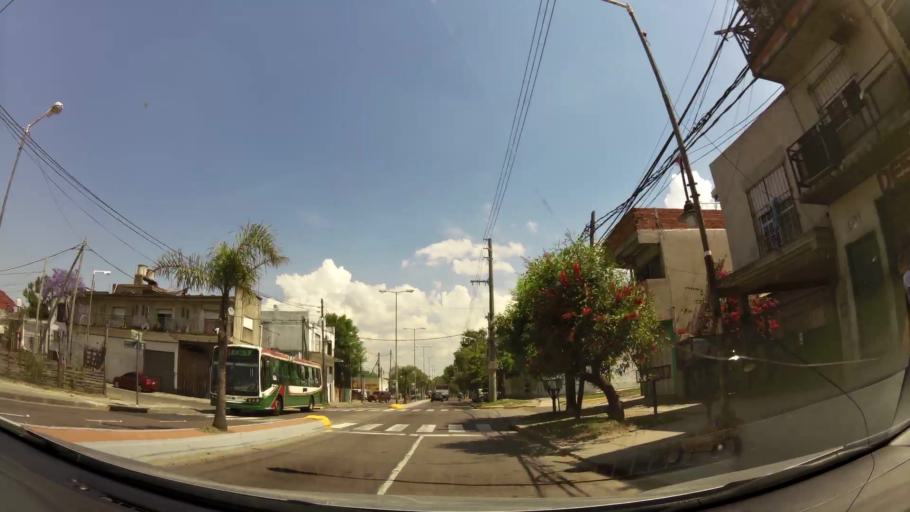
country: AR
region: Buenos Aires
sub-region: Partido de Tigre
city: Tigre
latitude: -34.4727
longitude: -58.5973
